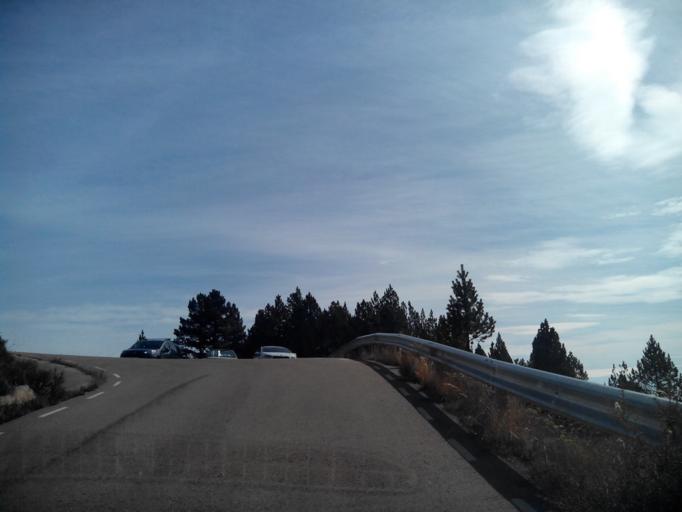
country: ES
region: Catalonia
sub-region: Provincia de Barcelona
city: Vallcebre
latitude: 42.2011
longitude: 1.7835
